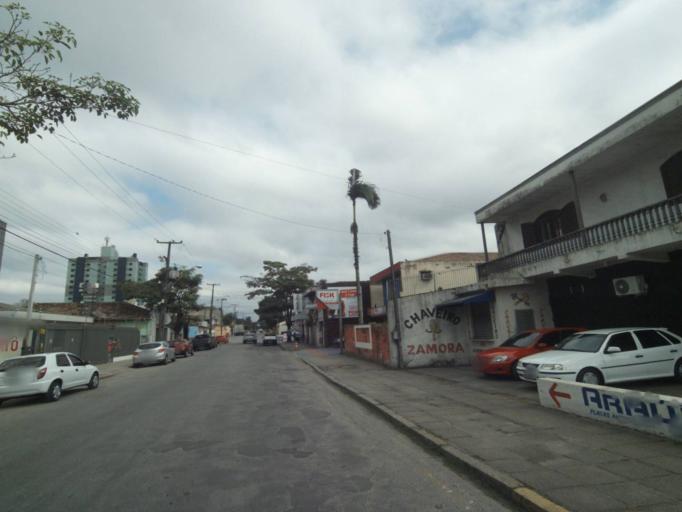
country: BR
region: Parana
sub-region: Paranagua
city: Paranagua
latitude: -25.5195
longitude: -48.5108
